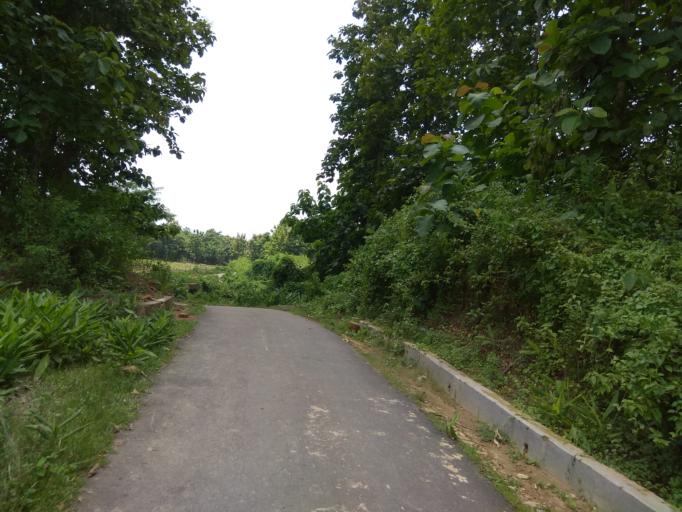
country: BD
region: Chittagong
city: Manikchari
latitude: 22.8905
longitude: 91.9220
